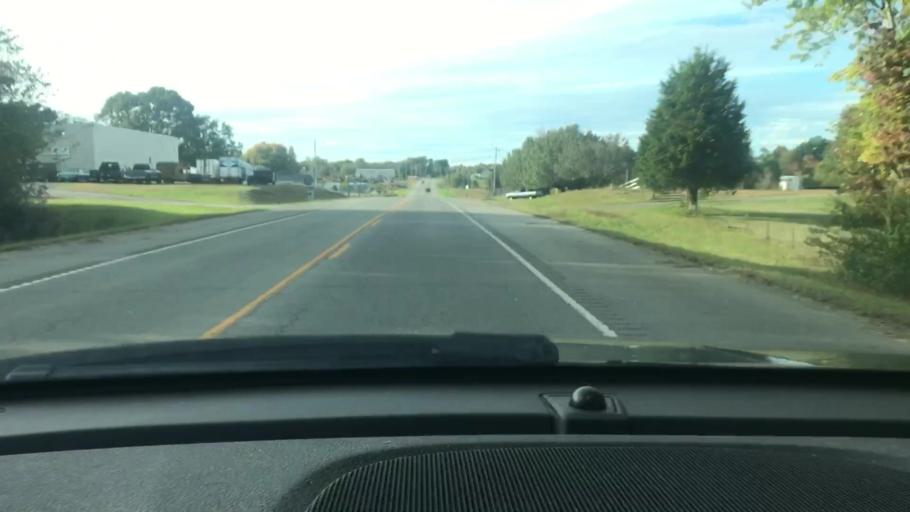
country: US
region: Tennessee
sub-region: Dickson County
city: White Bluff
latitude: 36.1295
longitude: -87.2305
